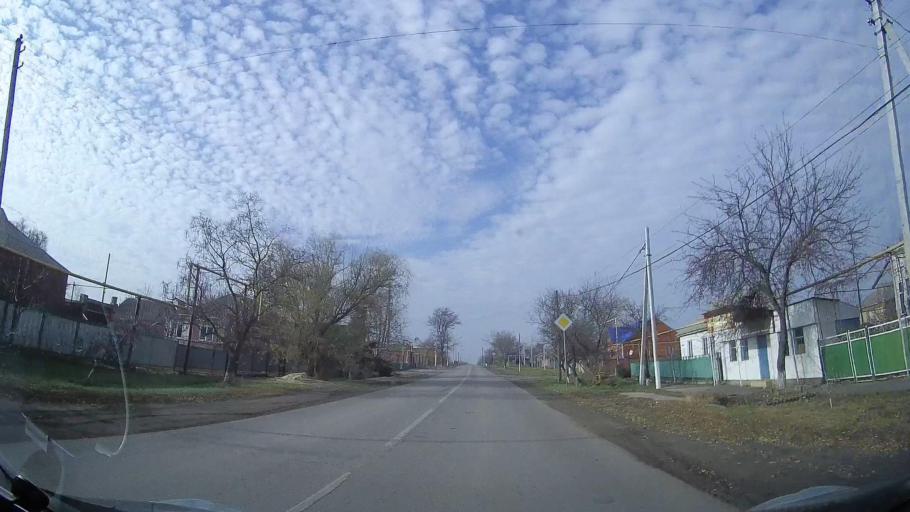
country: RU
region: Rostov
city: Veselyy
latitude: 47.0866
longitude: 40.7585
